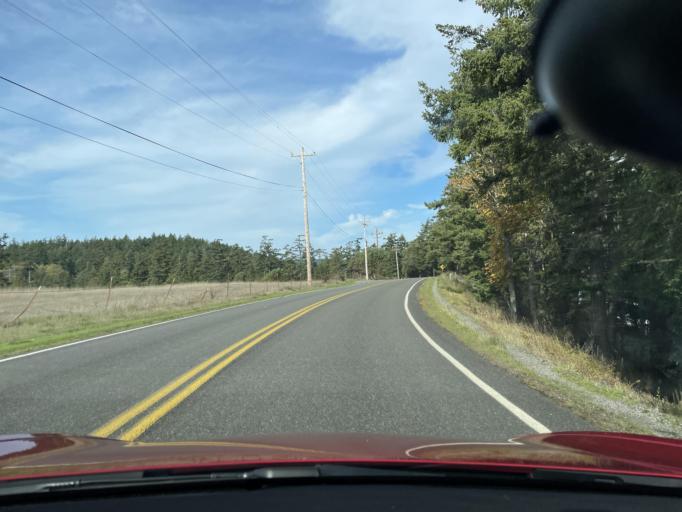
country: US
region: Washington
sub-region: San Juan County
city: Friday Harbor
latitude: 48.5258
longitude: -123.0011
